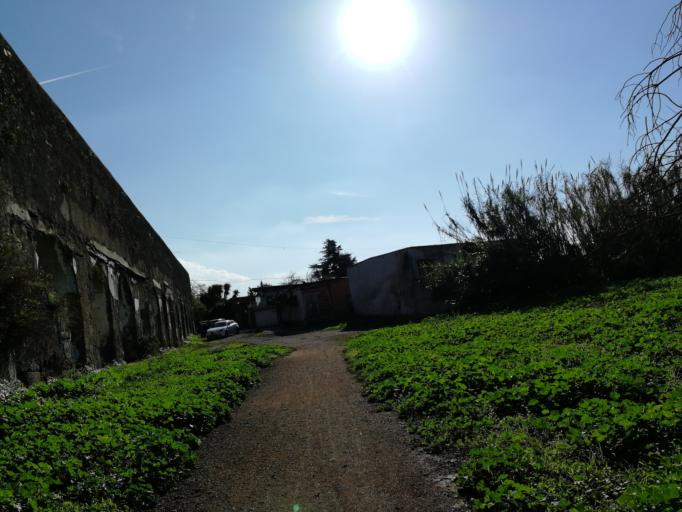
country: IT
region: Latium
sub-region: Citta metropolitana di Roma Capitale
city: Rome
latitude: 41.8577
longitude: 12.5448
